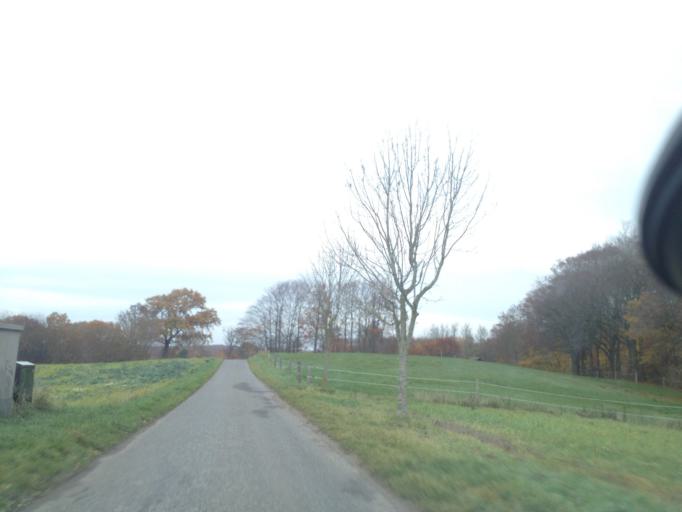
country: DK
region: South Denmark
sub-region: Assens Kommune
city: Vissenbjerg
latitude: 55.4324
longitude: 10.1660
